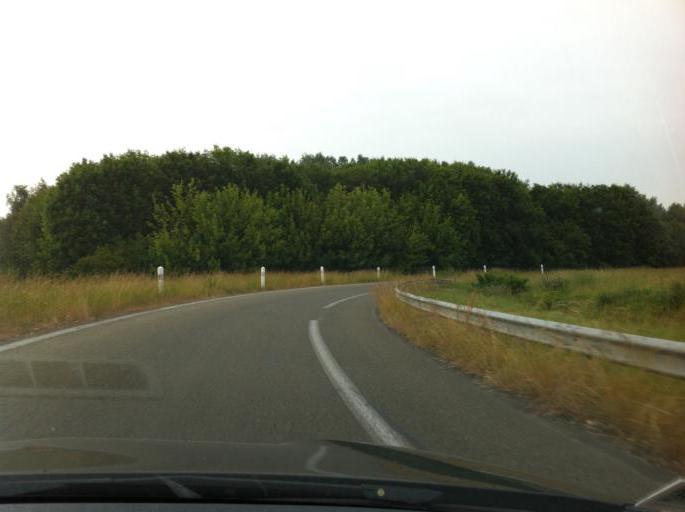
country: FR
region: Ile-de-France
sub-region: Departement de Seine-et-Marne
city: Moissy-Cramayel
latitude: 48.6121
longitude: 2.6324
